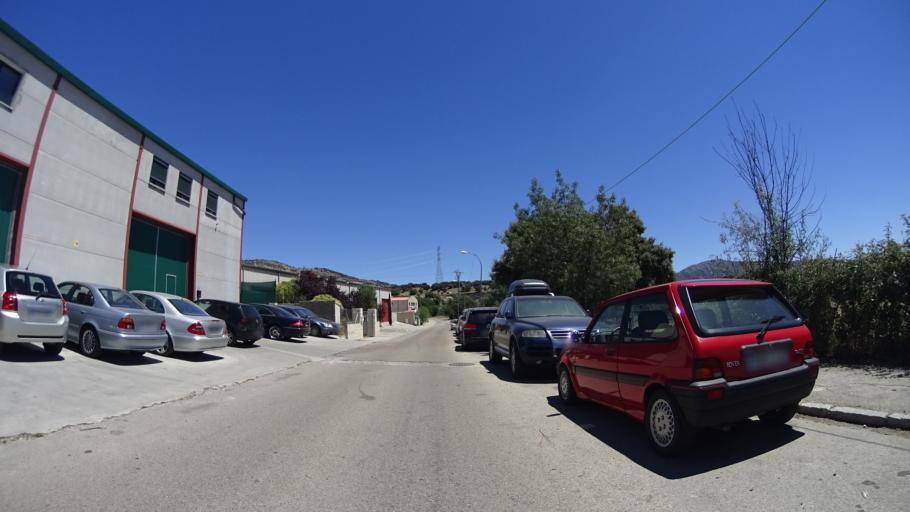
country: ES
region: Madrid
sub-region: Provincia de Madrid
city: Alpedrete
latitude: 40.6589
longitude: -4.0149
